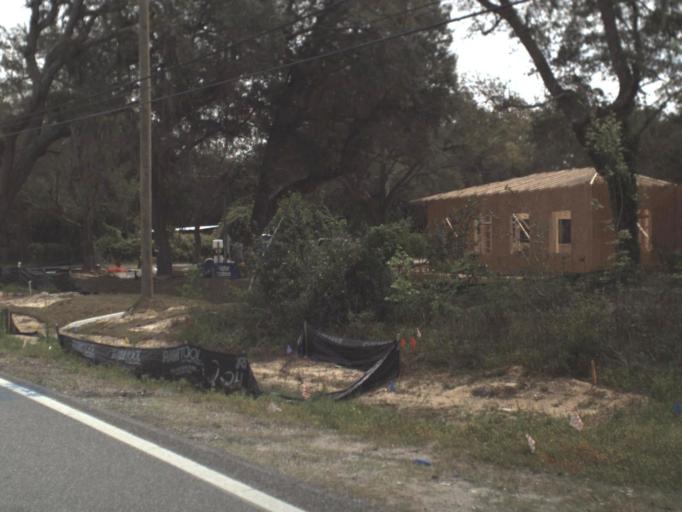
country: US
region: Florida
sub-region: Santa Rosa County
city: Tiger Point
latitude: 30.3956
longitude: -87.0274
